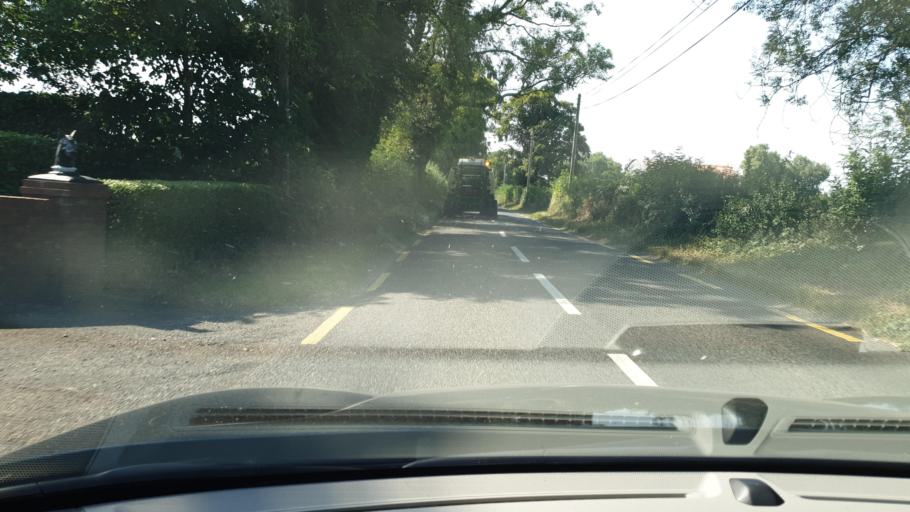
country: IE
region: Leinster
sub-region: An Mhi
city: Trim
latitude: 53.5814
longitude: -6.8464
